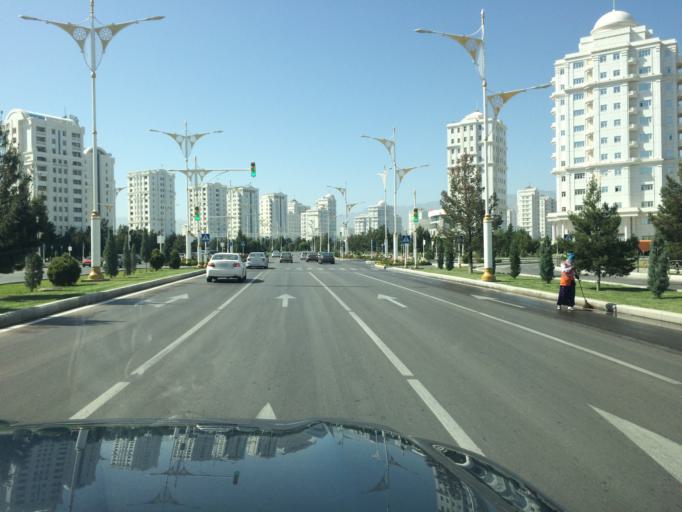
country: TM
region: Ahal
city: Ashgabat
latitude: 37.9078
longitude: 58.3653
